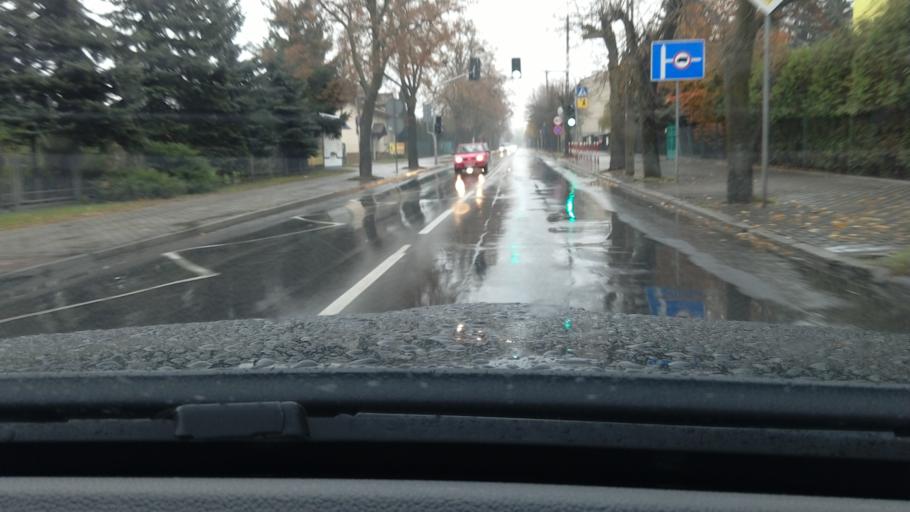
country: PL
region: Lodz Voivodeship
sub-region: Skierniewice
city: Skierniewice
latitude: 51.9534
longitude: 20.1355
